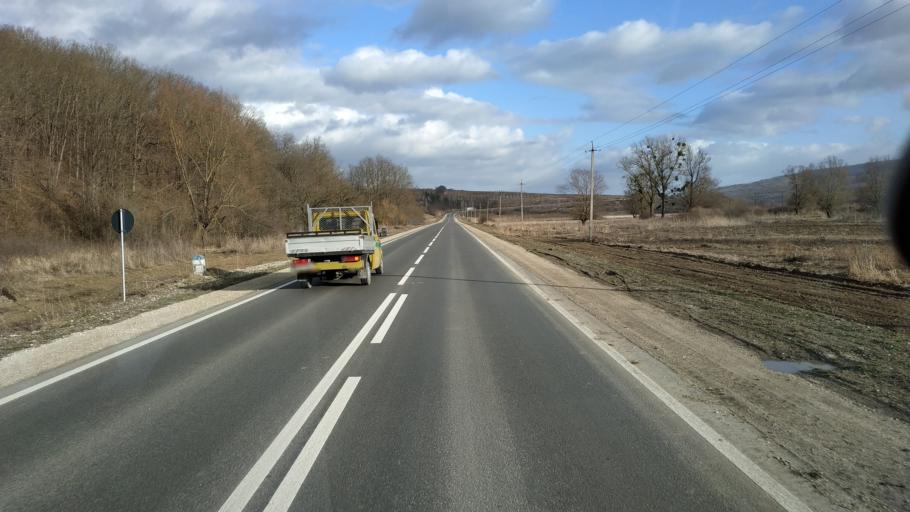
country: MD
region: Calarasi
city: Calarasi
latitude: 47.3022
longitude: 28.1424
